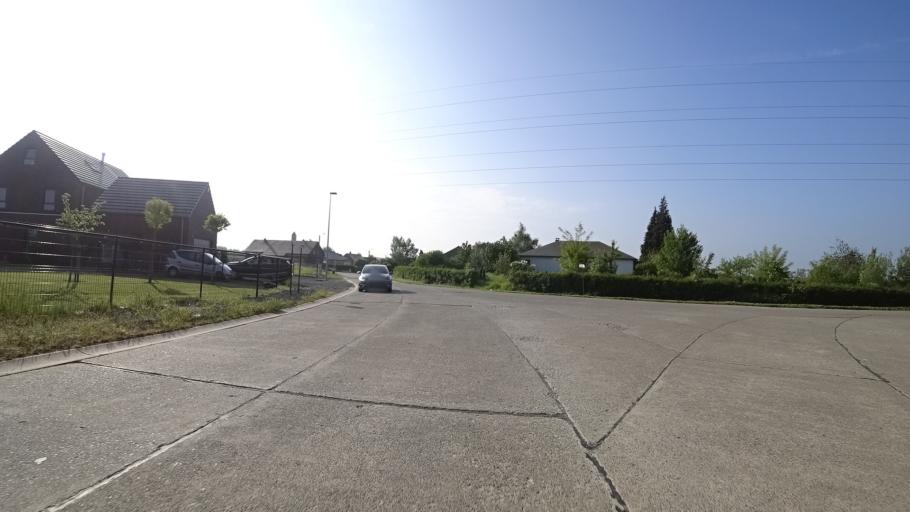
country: BE
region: Wallonia
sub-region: Province de Namur
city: Namur
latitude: 50.5211
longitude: 4.8255
